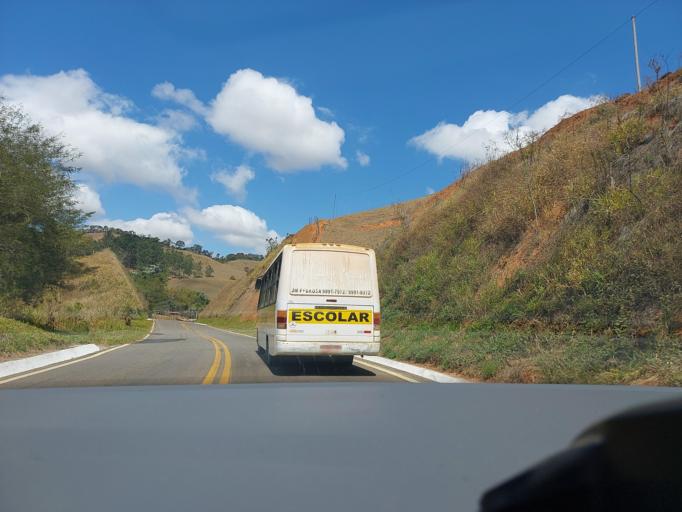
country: BR
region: Minas Gerais
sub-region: Muriae
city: Muriae
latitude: -21.0613
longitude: -42.5027
